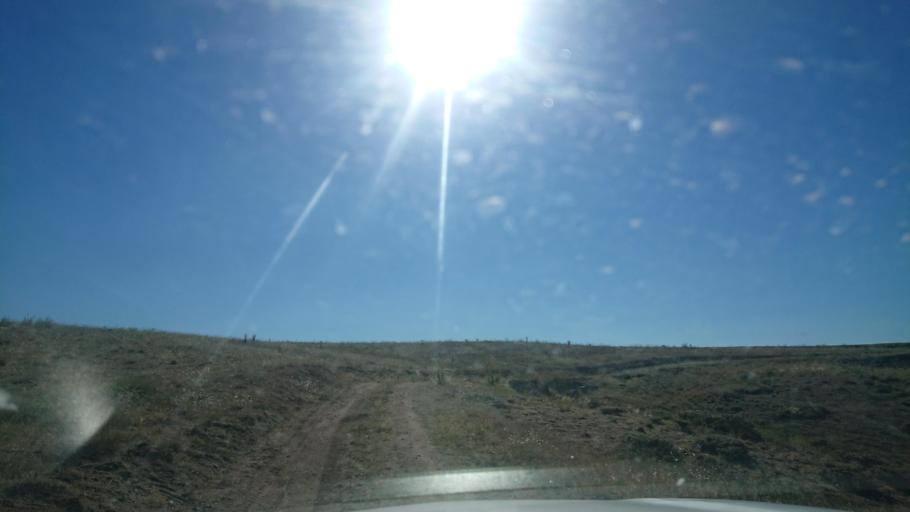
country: TR
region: Aksaray
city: Agacoren
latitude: 38.8377
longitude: 33.9366
